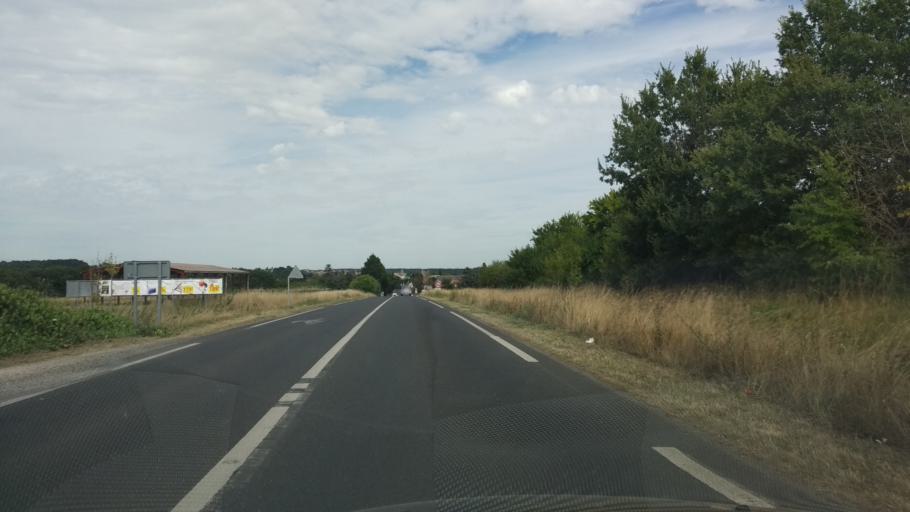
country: FR
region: Poitou-Charentes
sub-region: Departement de la Vienne
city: Chauvigny
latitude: 46.5675
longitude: 0.6224
